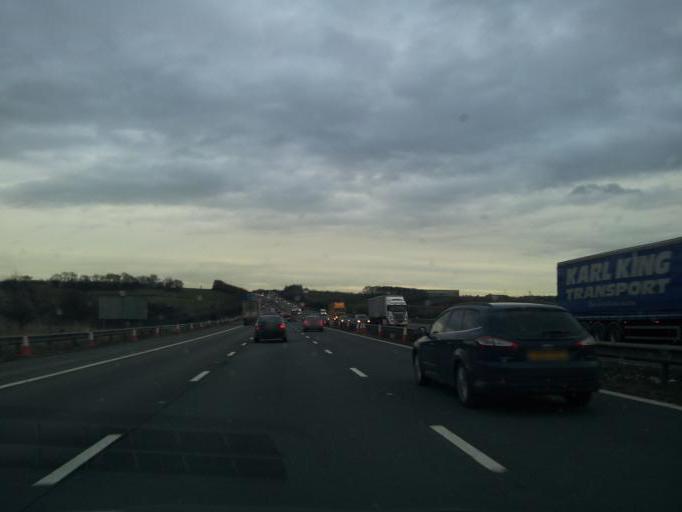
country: GB
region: England
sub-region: Warwickshire
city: Rugby
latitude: 52.4110
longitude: -1.2656
